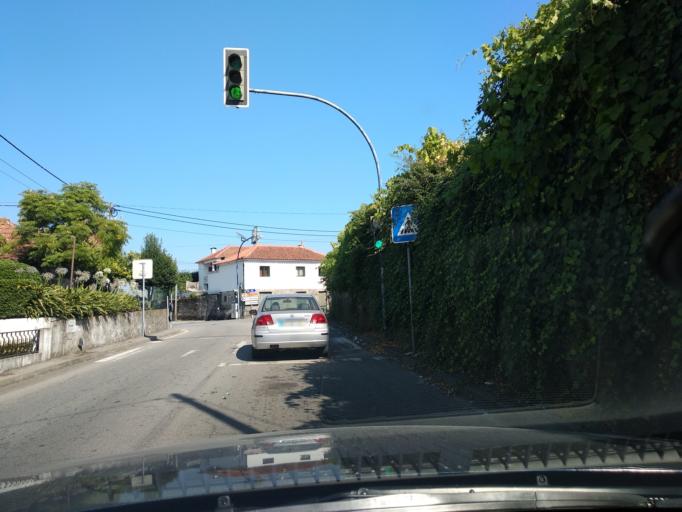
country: PT
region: Porto
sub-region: Paredes
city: Madalena
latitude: 41.2306
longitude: -8.3634
